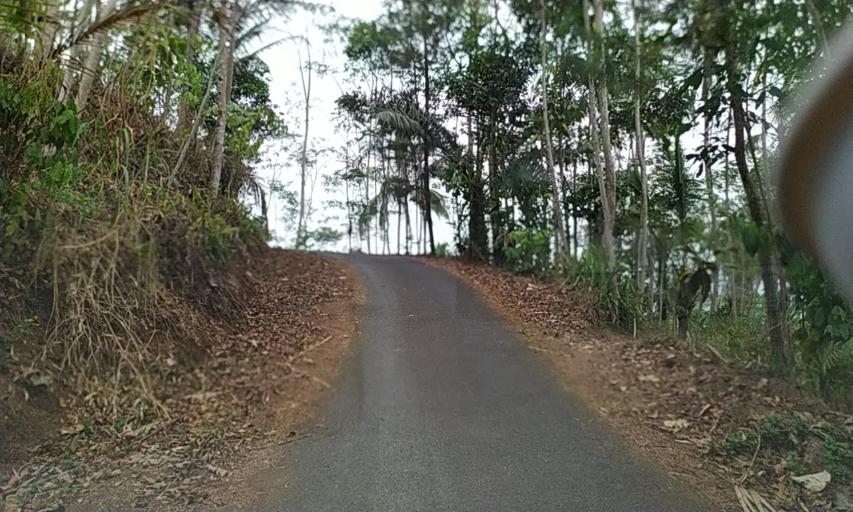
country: ID
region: Central Java
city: Ujungbarang Satu
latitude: -7.2105
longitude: 108.7726
